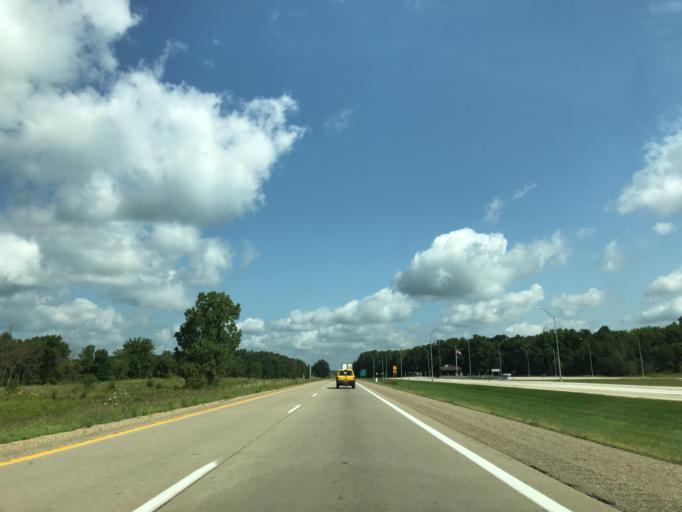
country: US
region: Michigan
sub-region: Branch County
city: Coldwater
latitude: 41.8751
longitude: -84.9906
